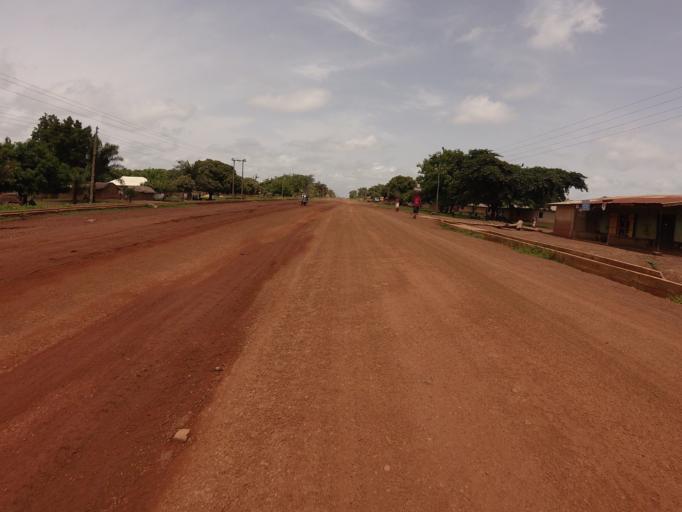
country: GH
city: Kpandae
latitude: 8.5914
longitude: 0.2373
